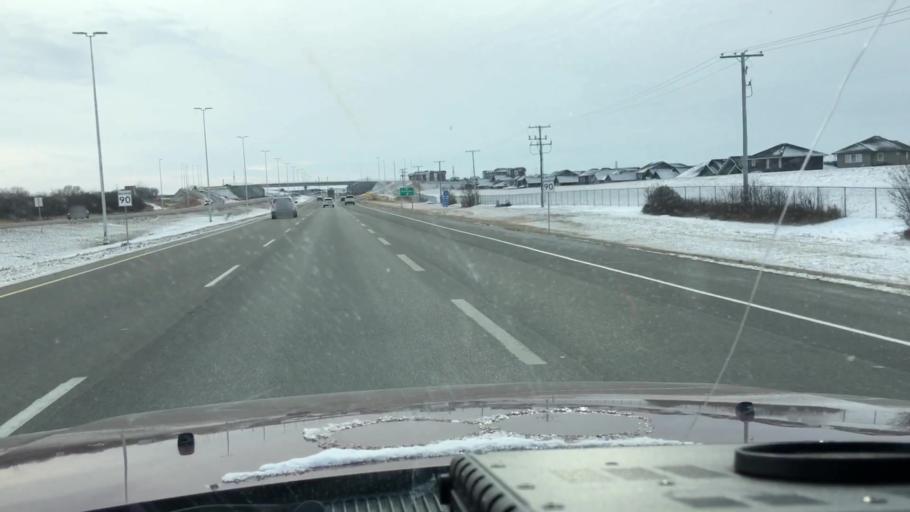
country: CA
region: Saskatchewan
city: Saskatoon
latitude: 52.0833
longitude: -106.6052
